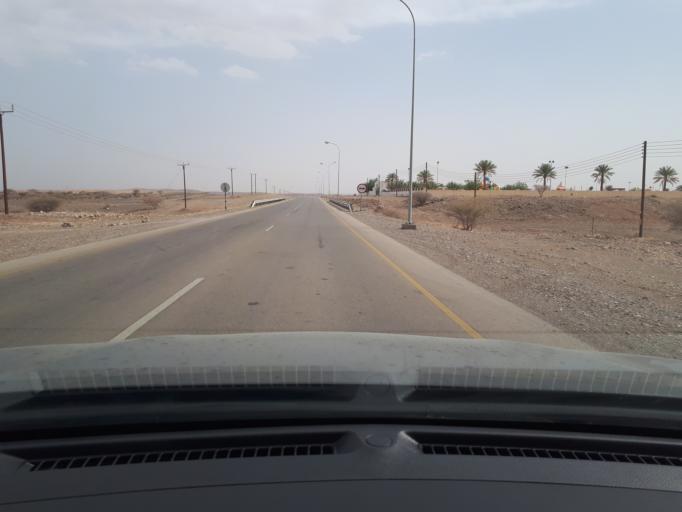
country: OM
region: Ash Sharqiyah
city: Badiyah
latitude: 22.5149
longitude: 58.9482
